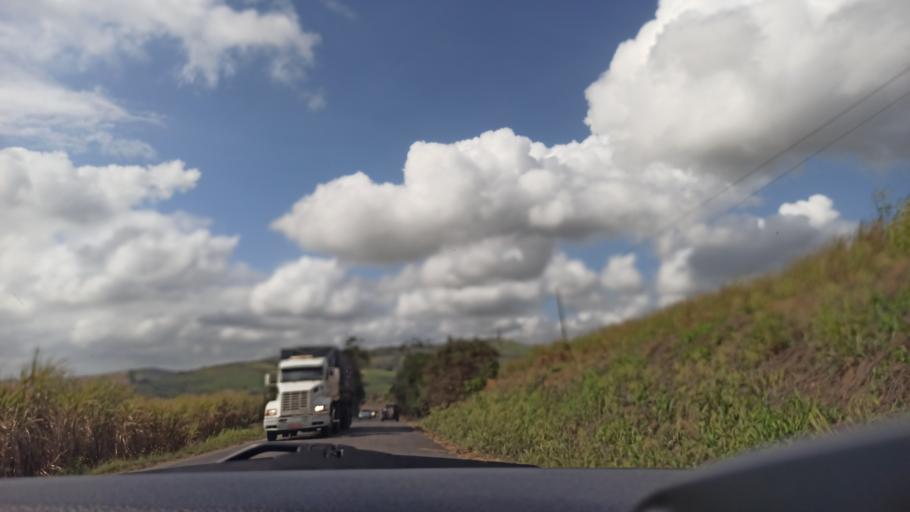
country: BR
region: Paraiba
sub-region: Juripiranga
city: Juripiranga
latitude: -7.4082
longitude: -35.2603
